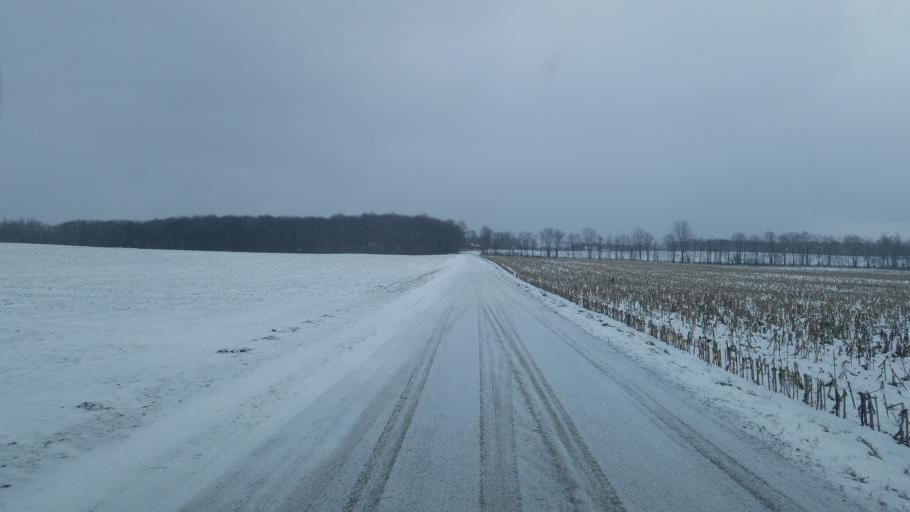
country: US
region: Pennsylvania
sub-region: Crawford County
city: Cochranton
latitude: 41.4441
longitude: -80.0122
